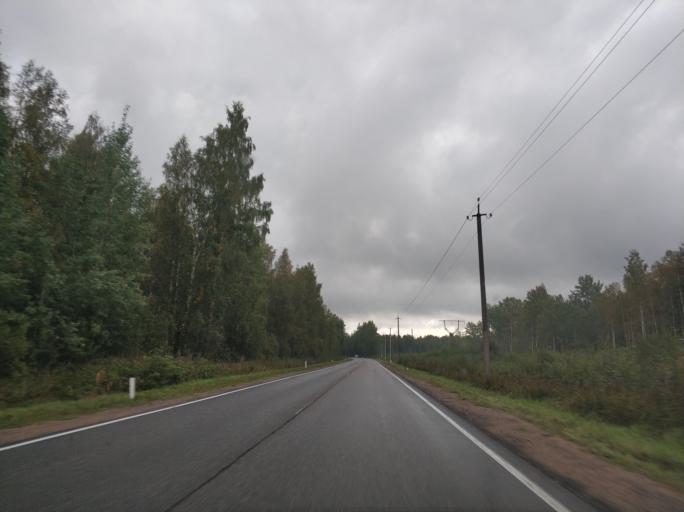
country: RU
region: Leningrad
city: Borisova Griva
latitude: 60.1121
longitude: 30.9623
